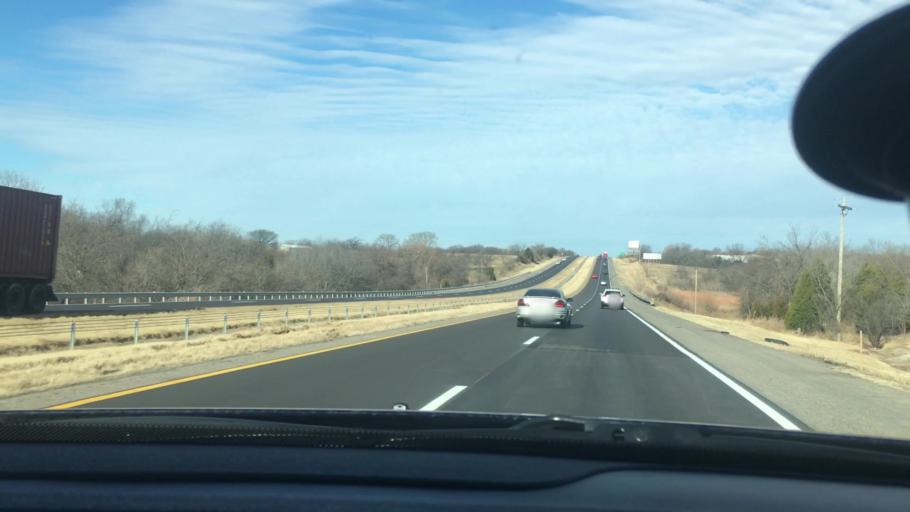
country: US
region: Oklahoma
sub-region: Cleveland County
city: Noble
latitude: 35.1016
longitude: -97.4289
